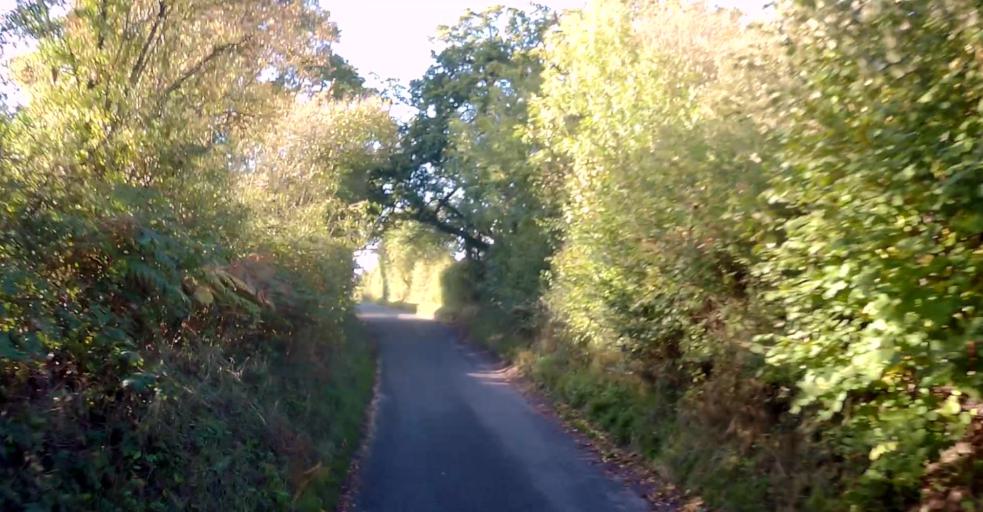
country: GB
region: England
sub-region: Hampshire
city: Long Sutton
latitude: 51.2120
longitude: -0.9082
